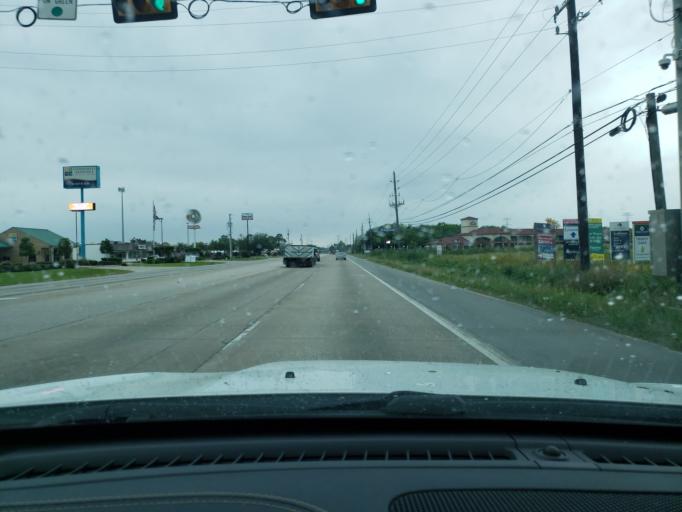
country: US
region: Texas
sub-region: Chambers County
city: Mont Belvieu
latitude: 29.8097
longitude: -94.9026
